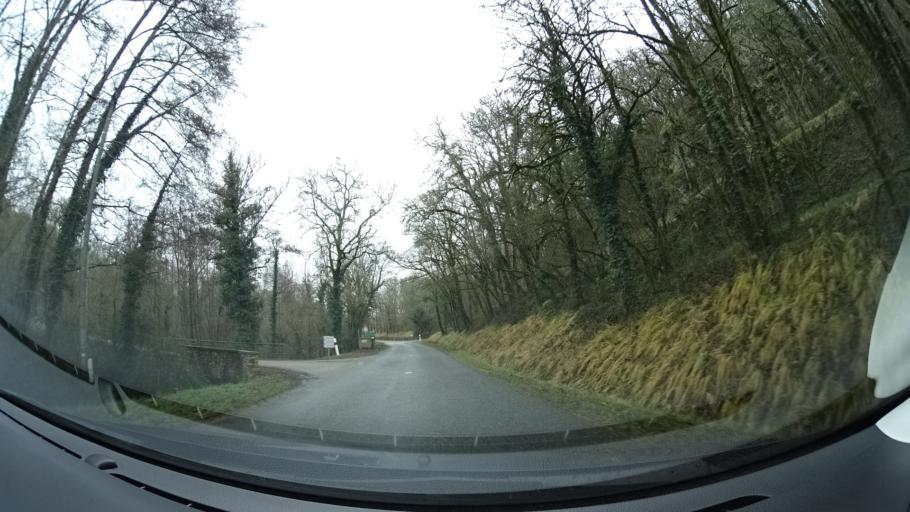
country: FR
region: Midi-Pyrenees
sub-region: Departement du Lot
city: Prayssac
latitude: 44.5835
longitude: 1.2347
